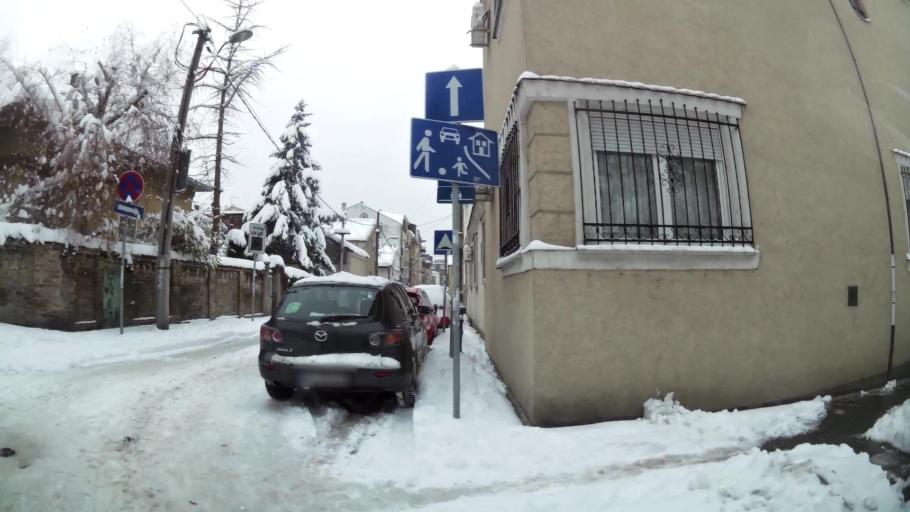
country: RS
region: Central Serbia
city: Belgrade
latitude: 44.8120
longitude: 20.4834
